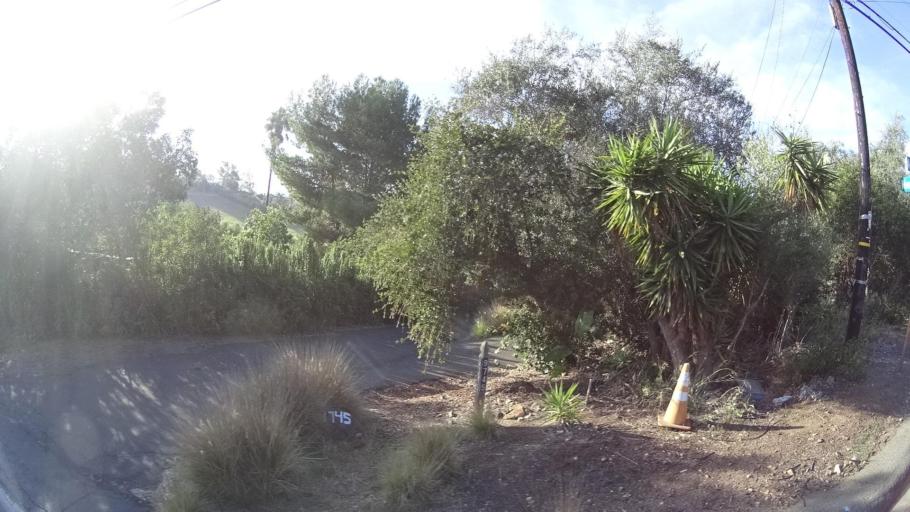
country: US
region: California
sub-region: San Diego County
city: Spring Valley
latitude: 32.7333
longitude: -116.9892
